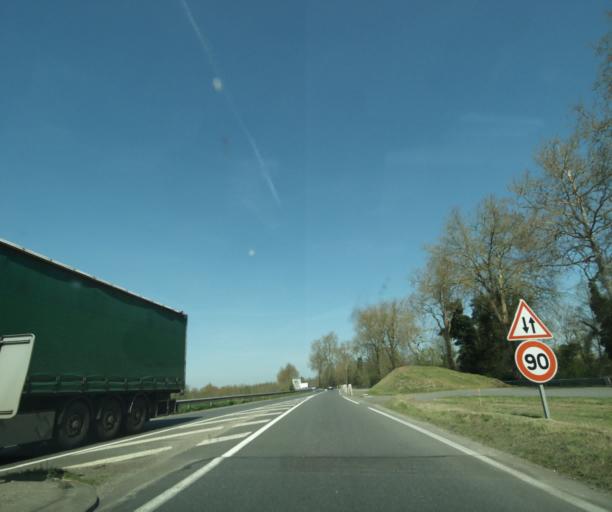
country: FR
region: Auvergne
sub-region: Departement de l'Allier
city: Trevol
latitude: 46.6254
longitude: 3.2859
